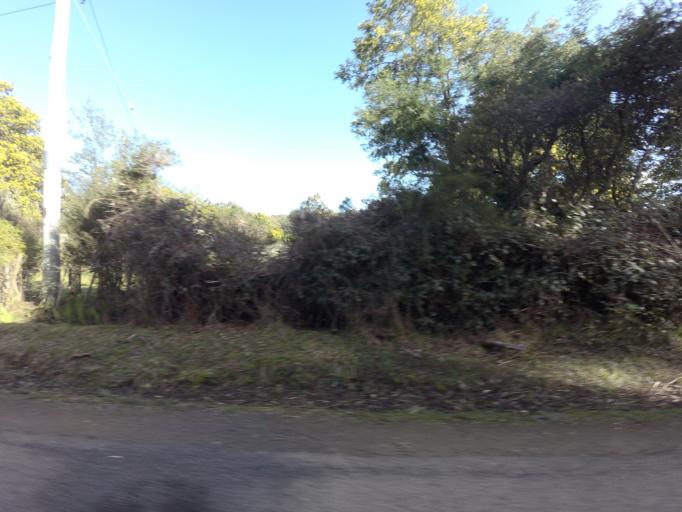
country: AU
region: Tasmania
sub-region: Kingborough
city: Kettering
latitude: -43.1092
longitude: 147.2560
